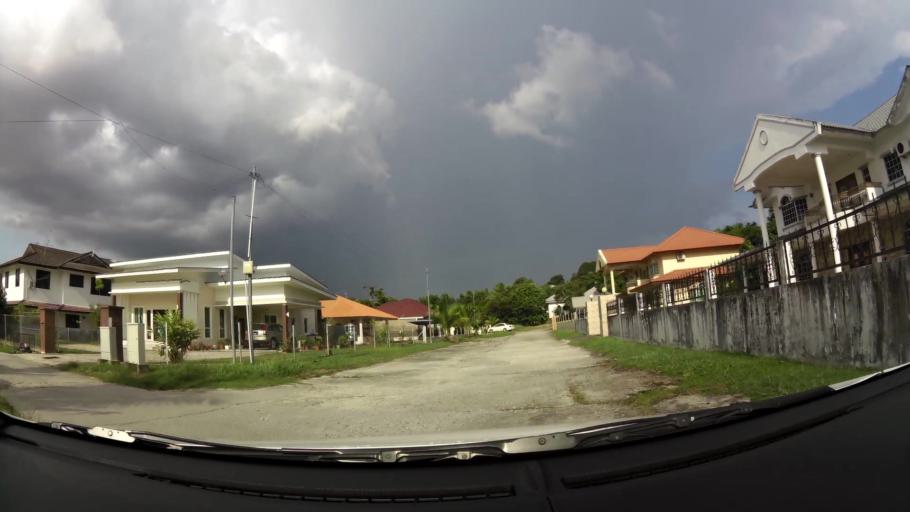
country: BN
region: Brunei and Muara
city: Bandar Seri Begawan
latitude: 4.9616
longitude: 114.9728
